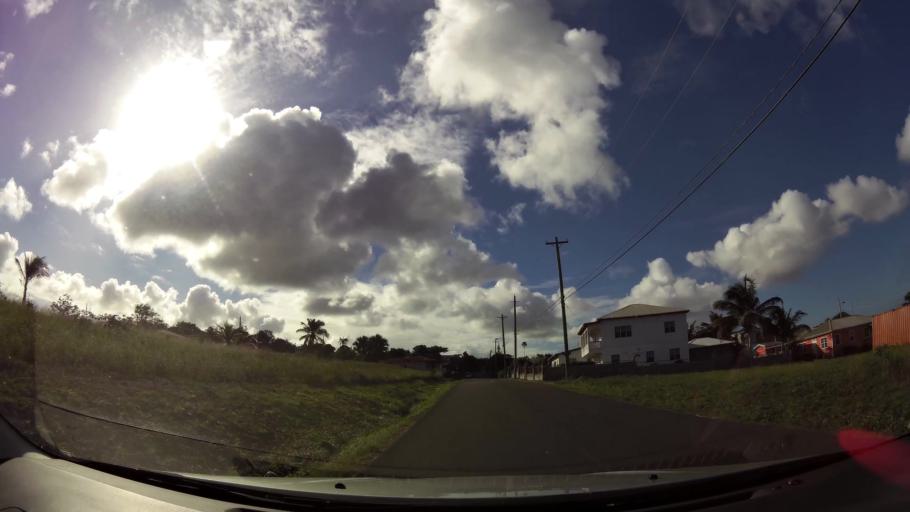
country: AG
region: Saint Peter
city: All Saints
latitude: 17.0788
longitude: -61.7834
